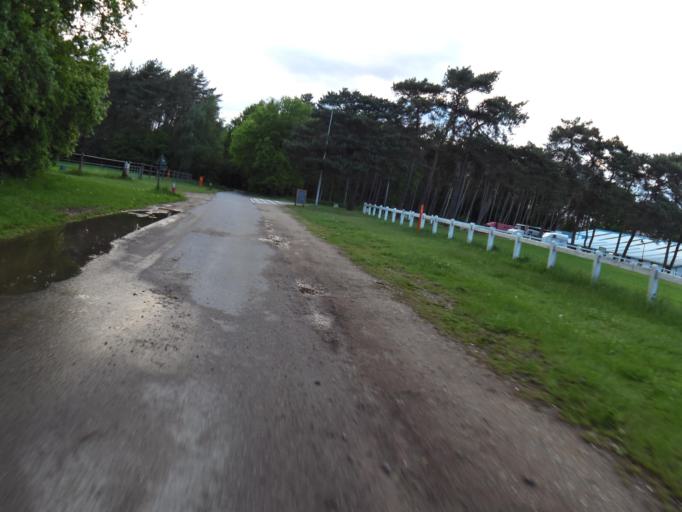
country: BE
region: Flanders
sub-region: Provincie Limburg
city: Zutendaal
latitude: 50.9433
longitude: 5.5527
